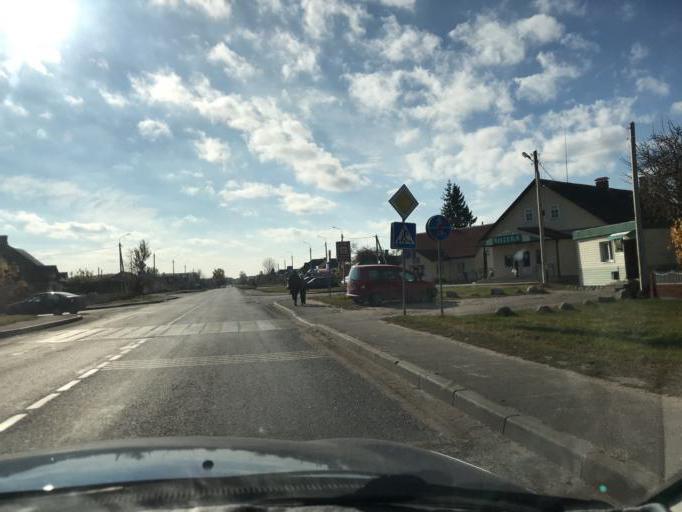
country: LT
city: Salcininkai
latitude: 54.2511
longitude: 25.3562
